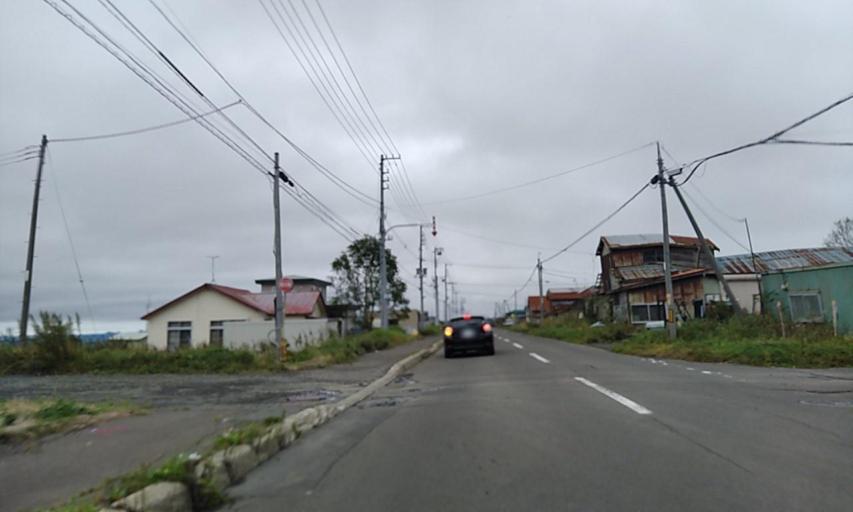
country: JP
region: Hokkaido
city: Nemuro
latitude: 43.3486
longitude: 145.5950
